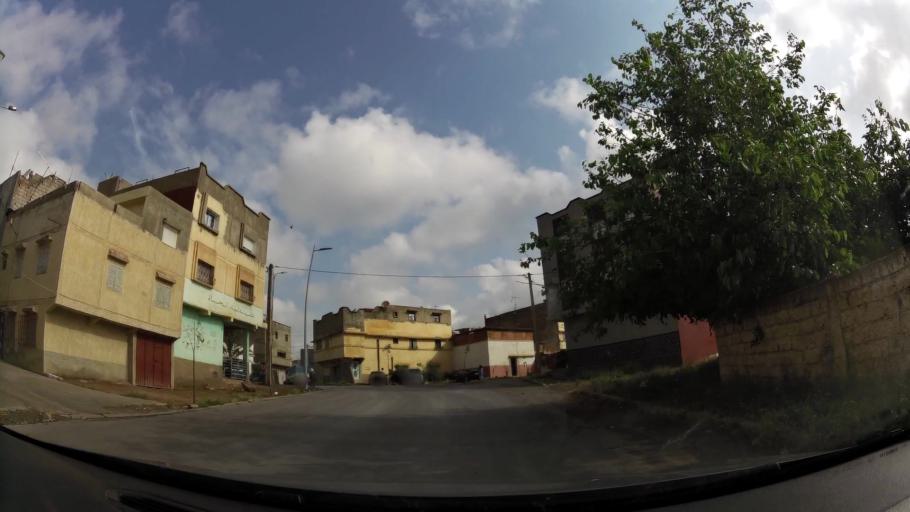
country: MA
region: Rabat-Sale-Zemmour-Zaer
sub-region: Khemisset
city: Tiflet
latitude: 33.8851
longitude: -6.3123
